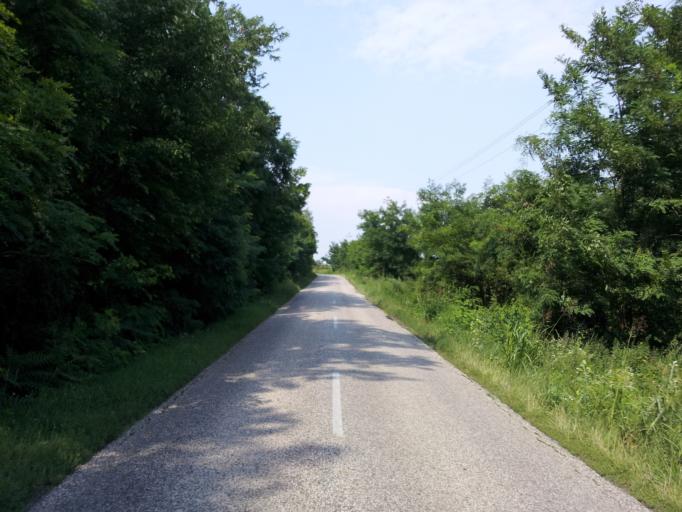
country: HU
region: Pest
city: Szigetujfalu
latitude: 47.2065
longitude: 18.9129
